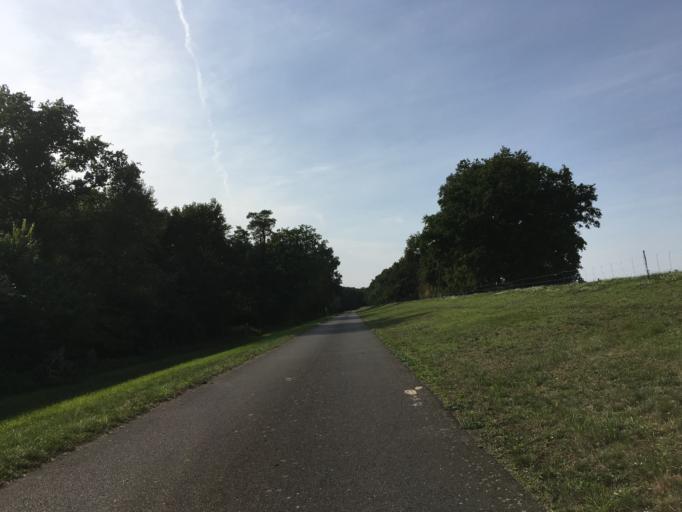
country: DE
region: Brandenburg
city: Brieskow-Finkenheerd
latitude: 52.2700
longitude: 14.6048
